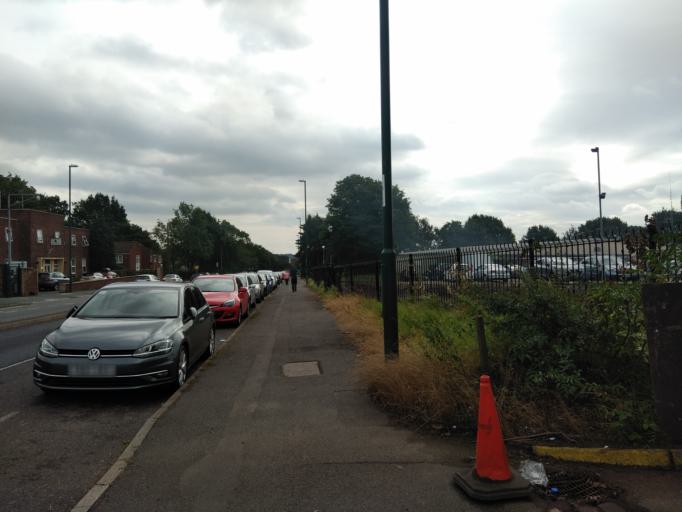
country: GB
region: England
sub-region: Nottinghamshire
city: Kimberley
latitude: 52.9685
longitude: -1.2099
